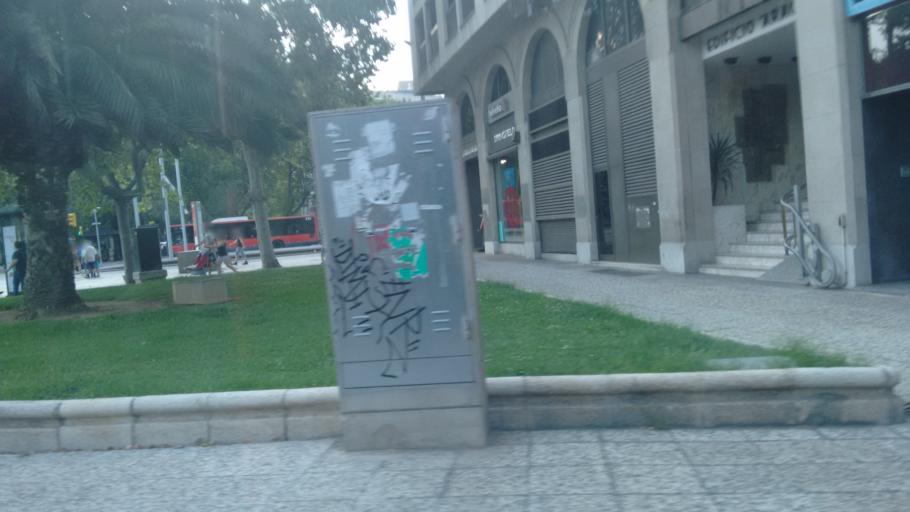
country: ES
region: Aragon
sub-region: Provincia de Zaragoza
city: Zaragoza
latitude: 41.6476
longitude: -0.8848
